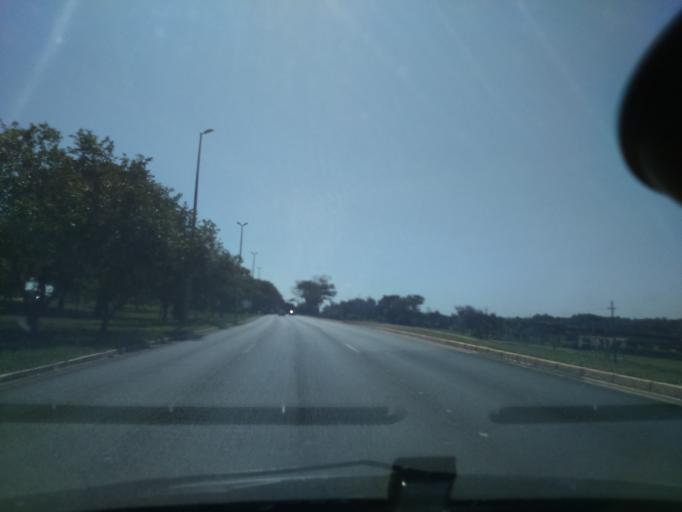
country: BR
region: Federal District
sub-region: Brasilia
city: Brasilia
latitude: -15.8336
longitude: -47.8946
